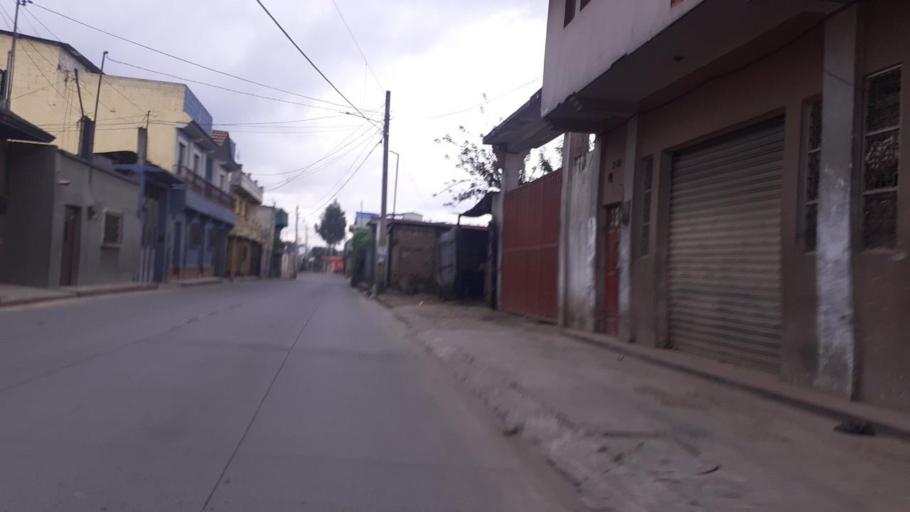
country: GT
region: Quetzaltenango
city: Ostuncalco
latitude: 14.8712
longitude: -91.6207
